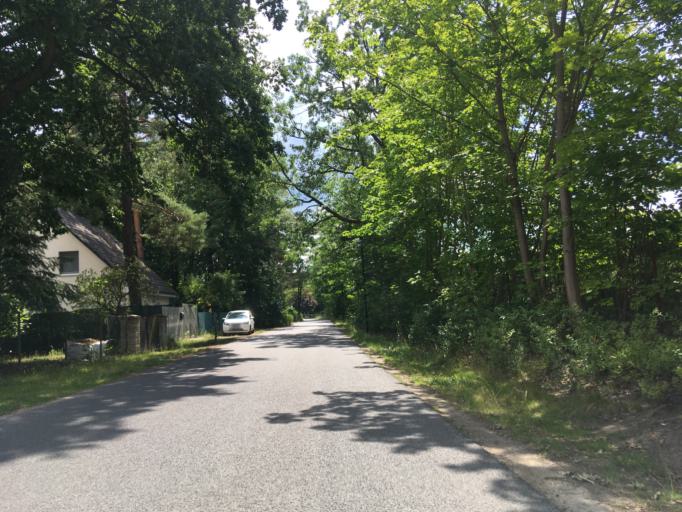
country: DE
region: Brandenburg
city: Wandlitz
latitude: 52.7449
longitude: 13.4665
